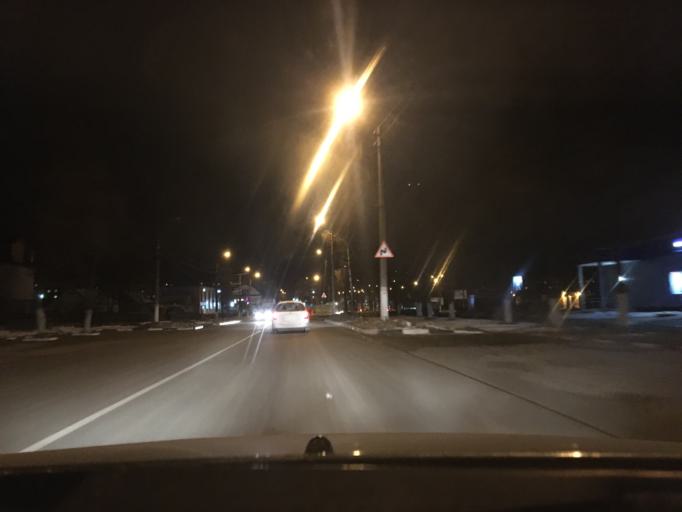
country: RU
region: Tula
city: Shchekino
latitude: 54.0197
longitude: 37.5042
